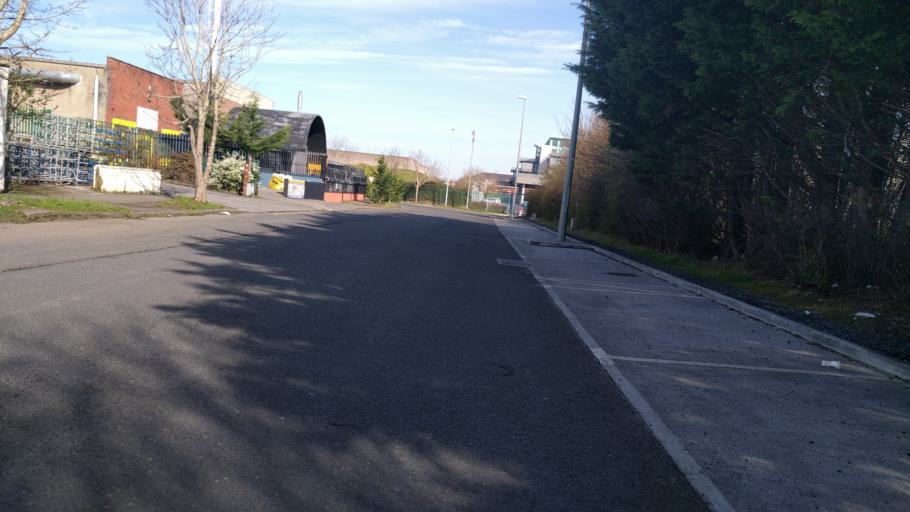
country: IE
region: Leinster
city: Tallaght
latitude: 53.2816
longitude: -6.3776
